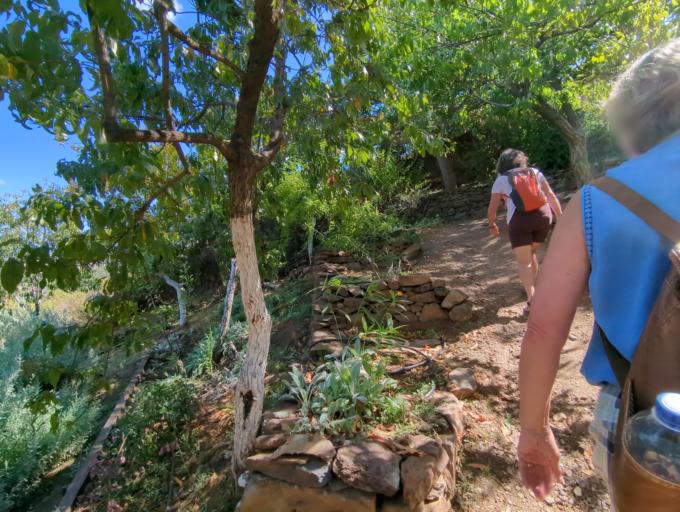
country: GR
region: Crete
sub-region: Nomos Chanias
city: Galatas
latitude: 35.4195
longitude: 23.9399
